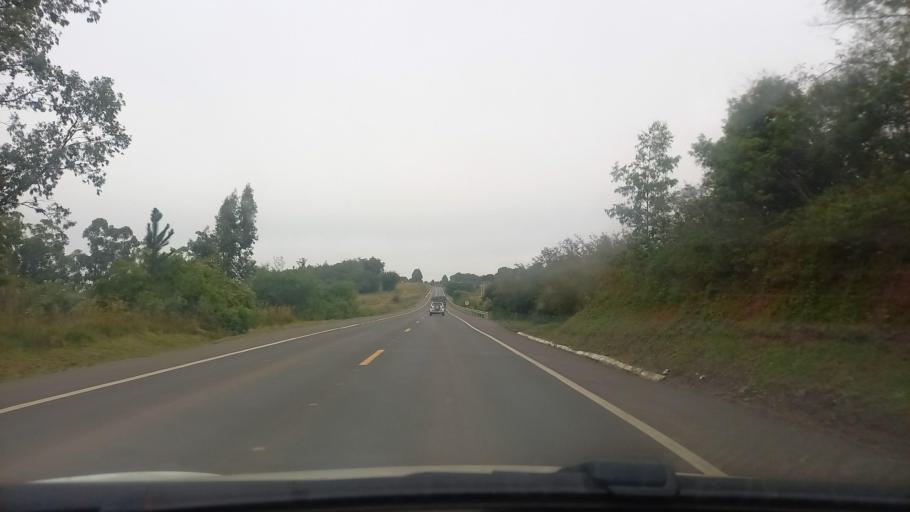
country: BR
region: Rio Grande do Sul
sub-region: Rosario Do Sul
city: Rosario do Sul
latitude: -30.2630
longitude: -54.9694
